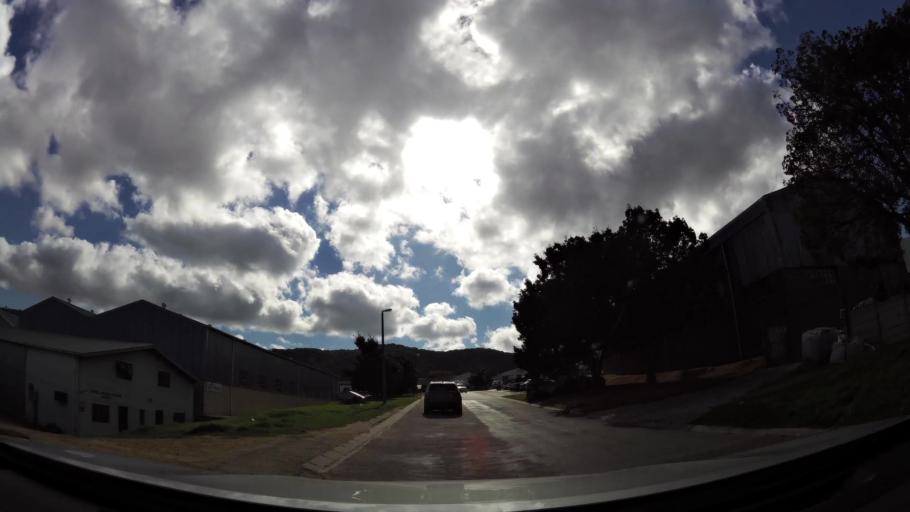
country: ZA
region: Western Cape
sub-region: Eden District Municipality
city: Knysna
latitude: -34.0447
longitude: 23.0805
